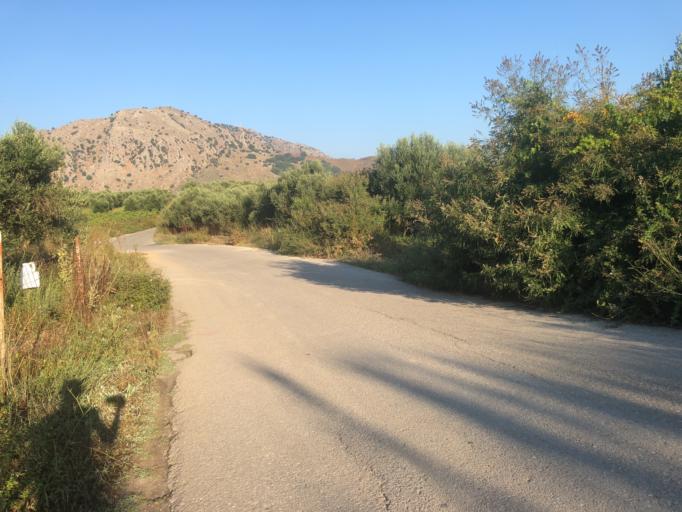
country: GR
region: Crete
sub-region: Nomos Chanias
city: Georgioupolis
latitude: 35.3382
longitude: 24.2879
